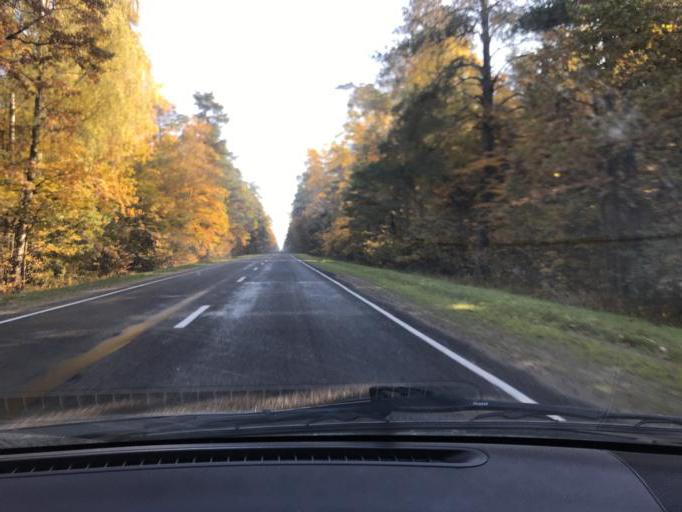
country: BY
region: Brest
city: Lyakhavichy
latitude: 52.9496
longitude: 26.1477
